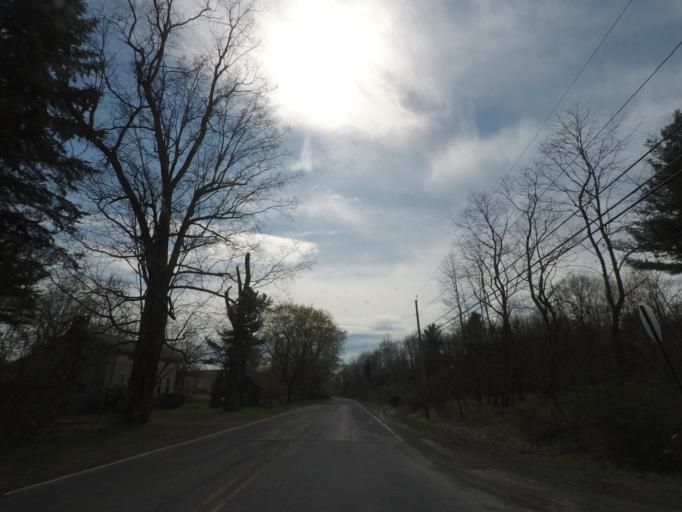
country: US
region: New York
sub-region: Columbia County
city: Chatham
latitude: 42.3533
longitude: -73.5594
